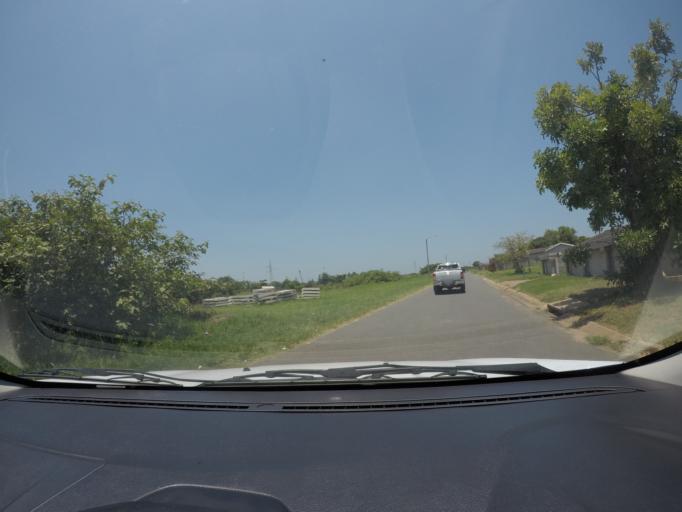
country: ZA
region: KwaZulu-Natal
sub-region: uThungulu District Municipality
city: eSikhawini
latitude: -28.8788
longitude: 31.8929
